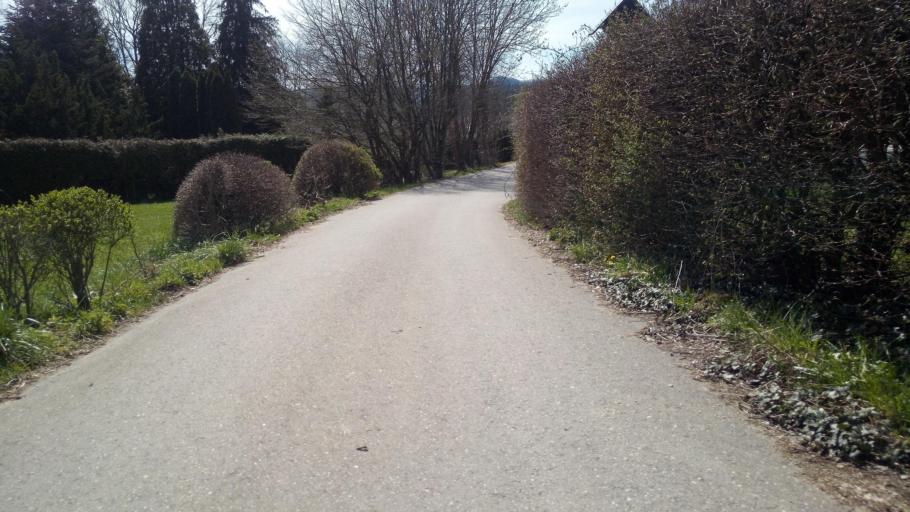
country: DE
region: Baden-Wuerttemberg
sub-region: Regierungsbezirk Stuttgart
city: Donzdorf
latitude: 48.6947
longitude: 9.8135
